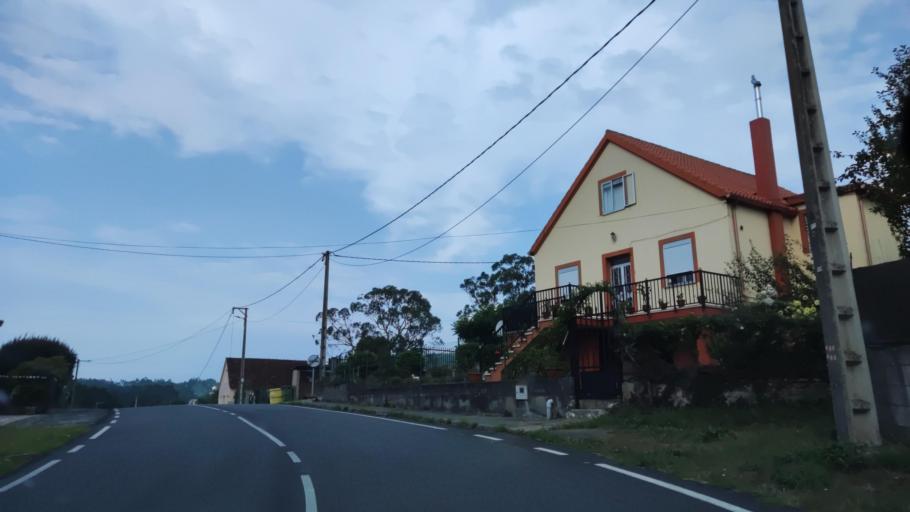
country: ES
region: Galicia
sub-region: Provincia de Pontevedra
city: Catoira
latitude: 42.6547
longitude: -8.7621
